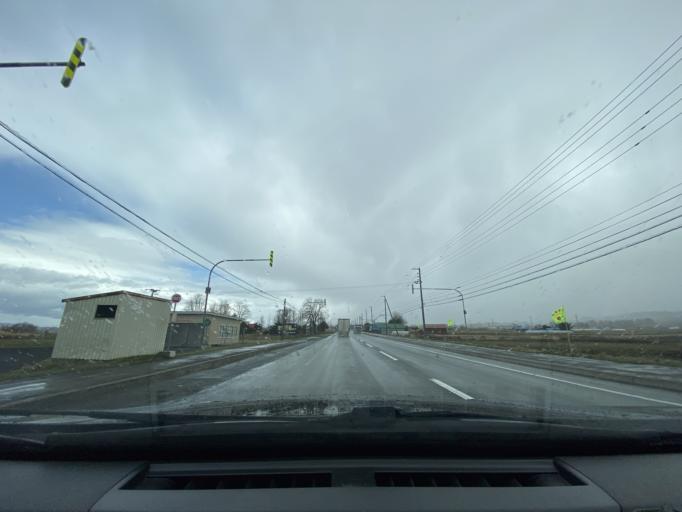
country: JP
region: Hokkaido
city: Fukagawa
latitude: 43.6807
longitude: 142.0376
